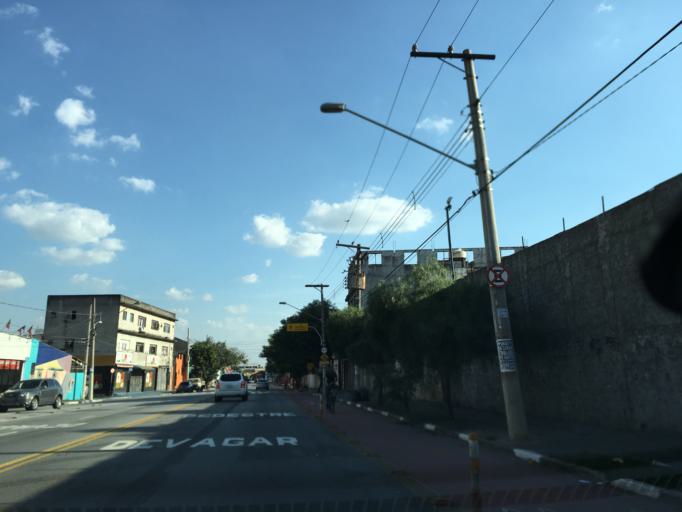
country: BR
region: Sao Paulo
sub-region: Sao Paulo
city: Sao Paulo
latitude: -23.4845
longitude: -46.6508
